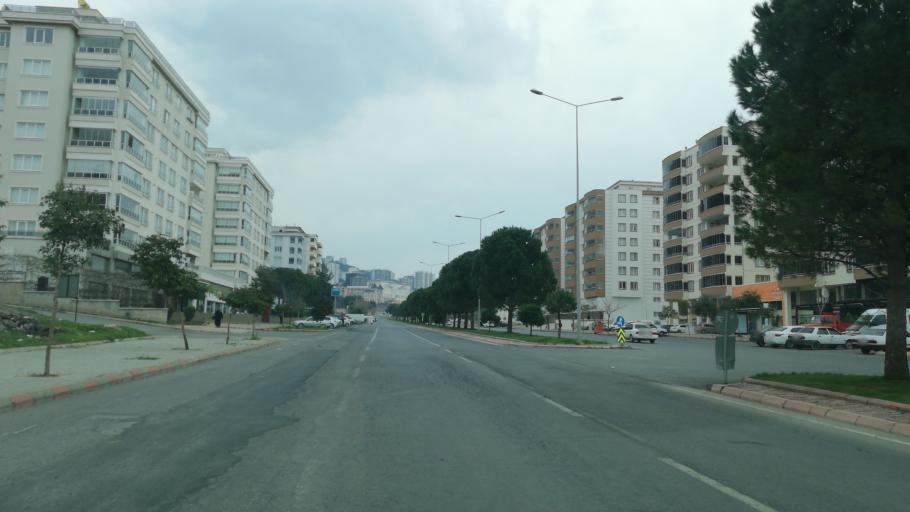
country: TR
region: Kahramanmaras
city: Kahramanmaras
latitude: 37.6000
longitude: 36.8263
